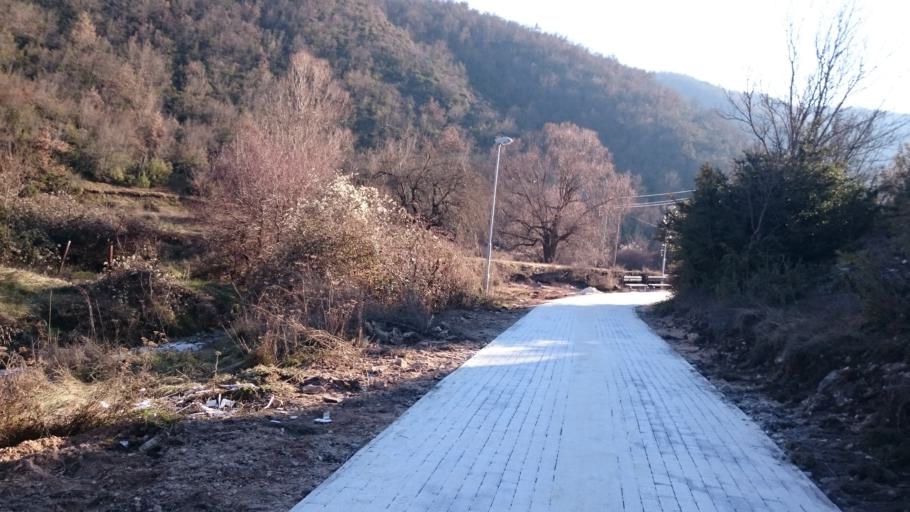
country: MK
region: Makedonski Brod
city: Makedonski Brod
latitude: 41.5436
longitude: 21.2459
